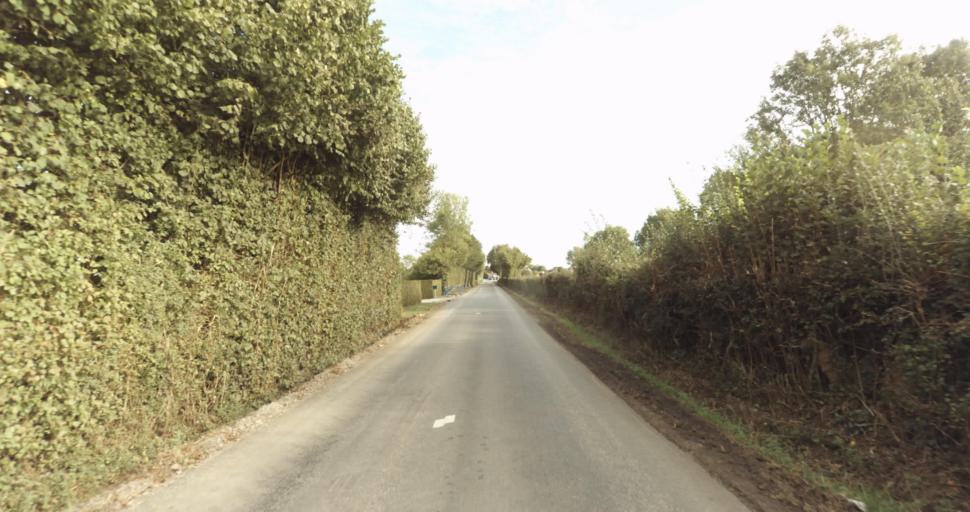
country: FR
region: Lower Normandy
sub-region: Departement de l'Orne
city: Gace
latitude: 48.8520
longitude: 0.2538
